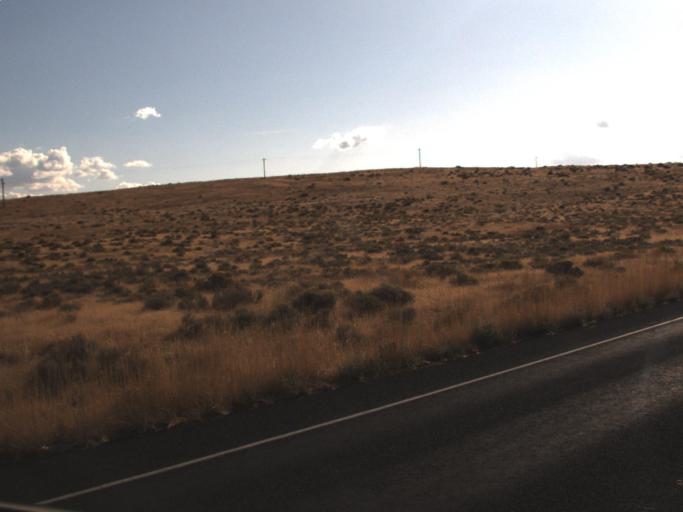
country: US
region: Oregon
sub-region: Morrow County
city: Boardman
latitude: 45.8838
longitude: -119.7226
